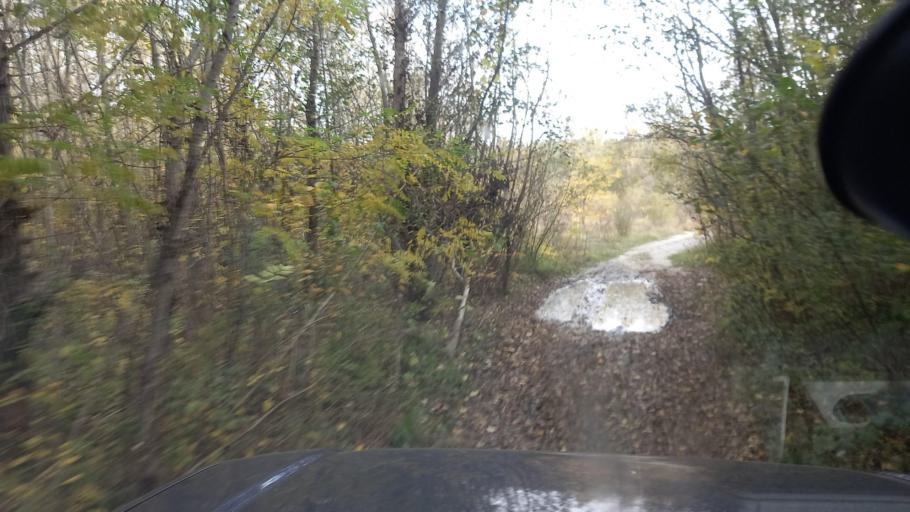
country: RU
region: Krasnodarskiy
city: Shedok
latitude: 44.1701
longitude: 40.8471
